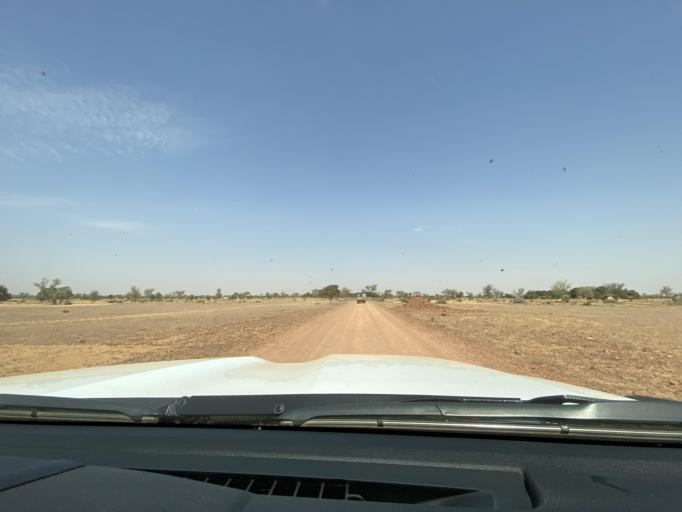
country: NE
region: Dosso
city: Birnin Gaoure
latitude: 13.2378
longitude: 2.8673
